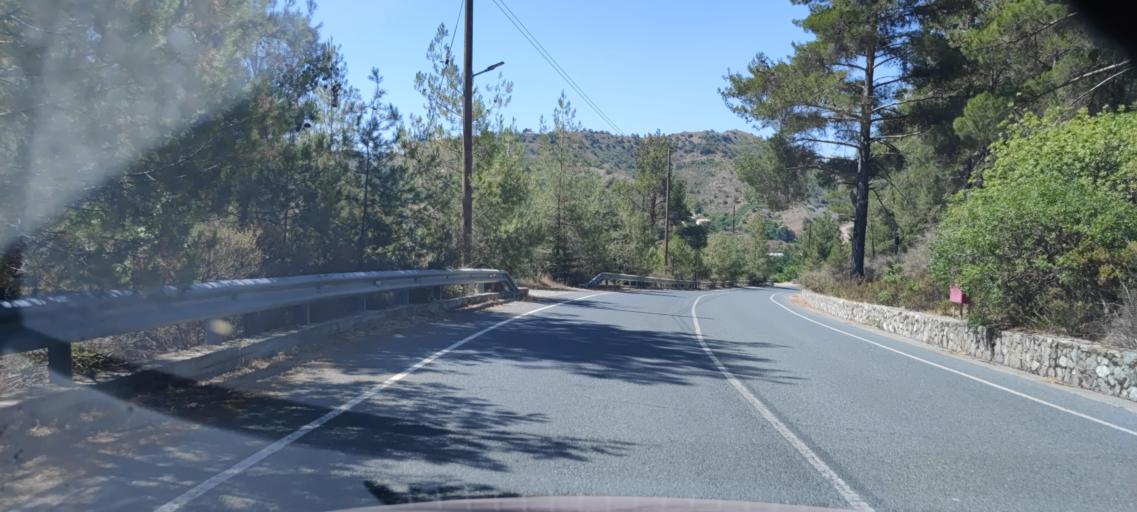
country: CY
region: Lefkosia
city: Kakopetria
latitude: 34.8975
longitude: 32.8362
